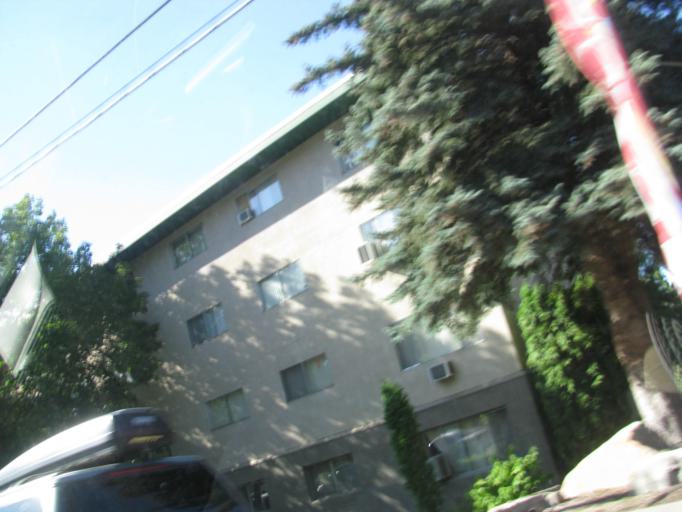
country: US
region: Washington
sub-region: Spokane County
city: Spokane
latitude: 47.6573
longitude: -117.4439
